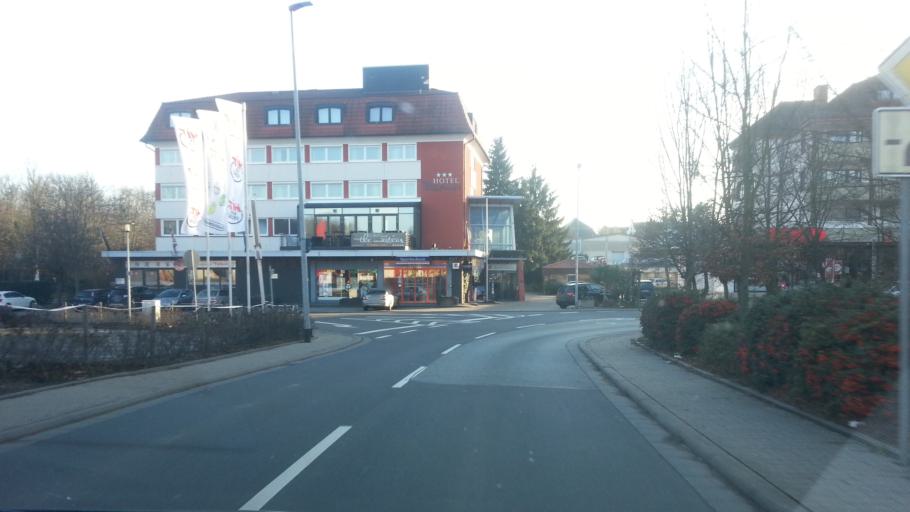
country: DE
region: Rheinland-Pfalz
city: Kirchheimbolanden
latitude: 49.6658
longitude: 8.0158
